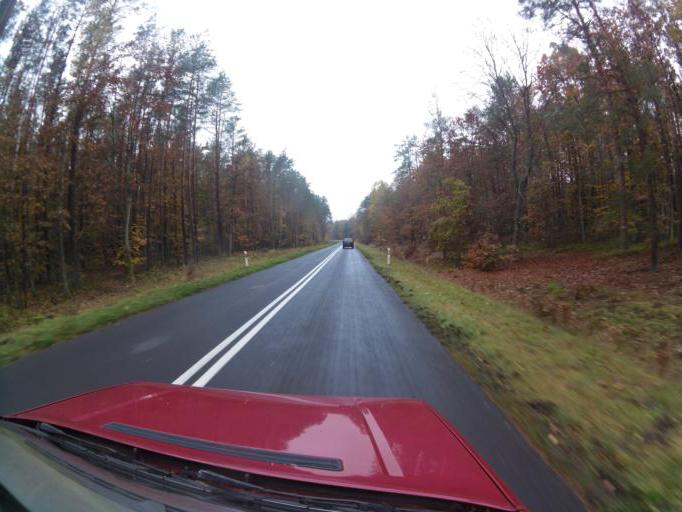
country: PL
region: West Pomeranian Voivodeship
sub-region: Powiat policki
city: Dobra
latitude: 53.5838
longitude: 14.3966
